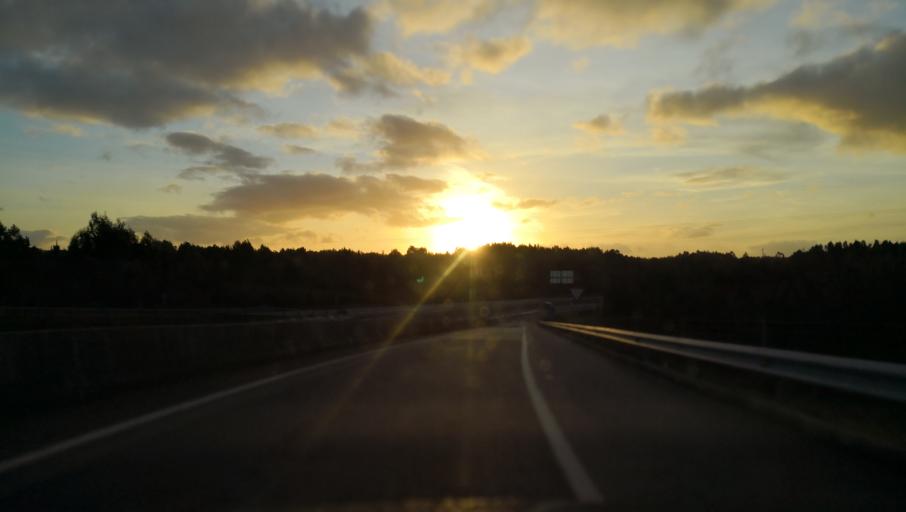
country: ES
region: Galicia
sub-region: Provincia da Coruna
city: Oroso
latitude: 42.9104
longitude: -8.4337
